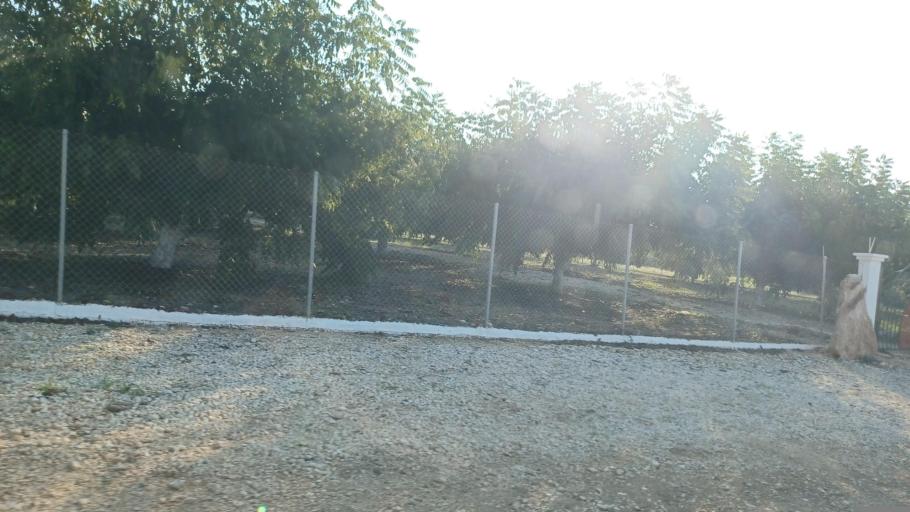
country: CY
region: Pafos
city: Pegeia
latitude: 34.9025
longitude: 32.3327
